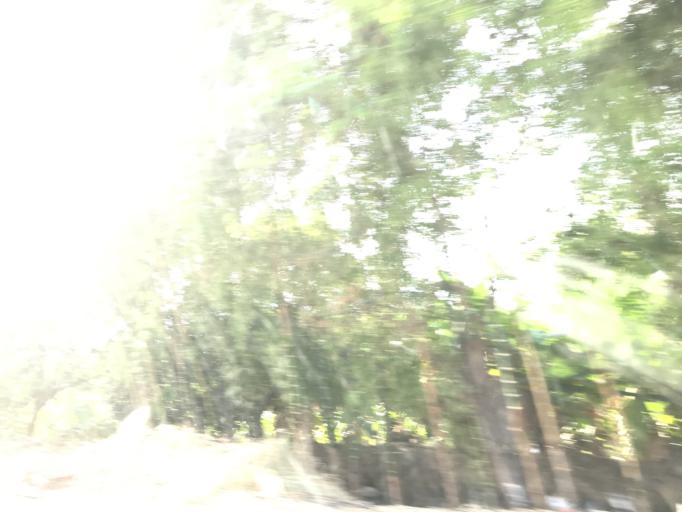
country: PE
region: Lambayeque
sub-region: Provincia de Chiclayo
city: Chongoyape
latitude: -6.6755
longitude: -79.4393
